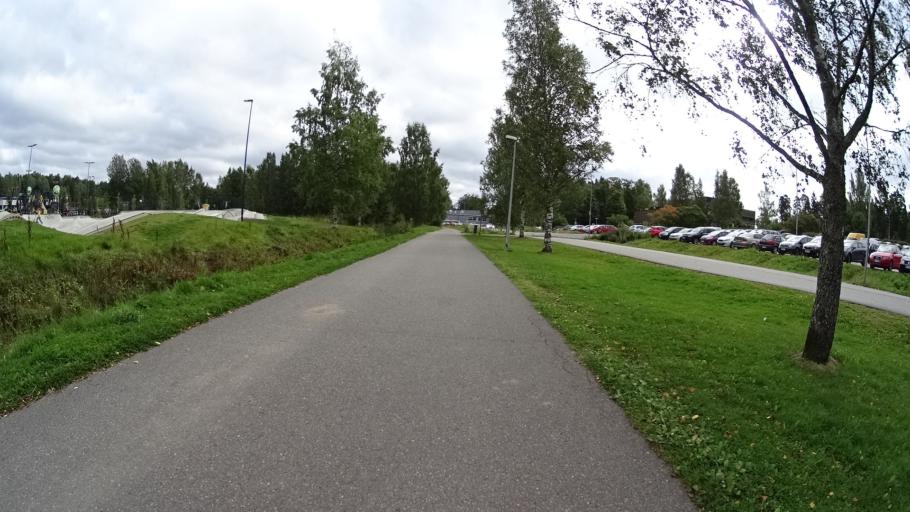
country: FI
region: Uusimaa
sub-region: Helsinki
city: Kilo
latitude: 60.2239
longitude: 24.8013
